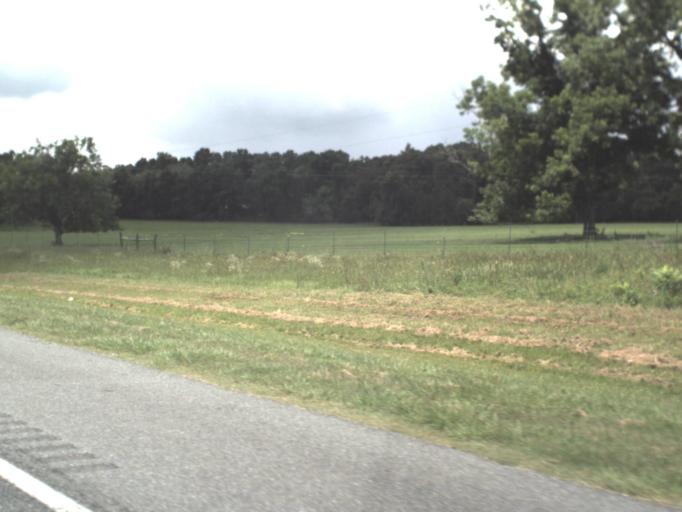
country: US
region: Florida
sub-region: Columbia County
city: Lake City
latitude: 30.1058
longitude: -82.6492
